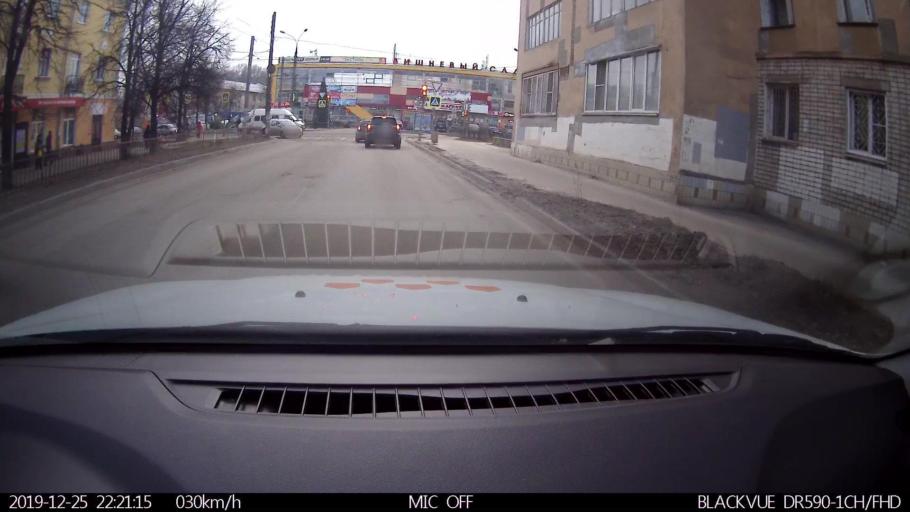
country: RU
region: Nizjnij Novgorod
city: Gorbatovka
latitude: 56.3320
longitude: 43.8400
